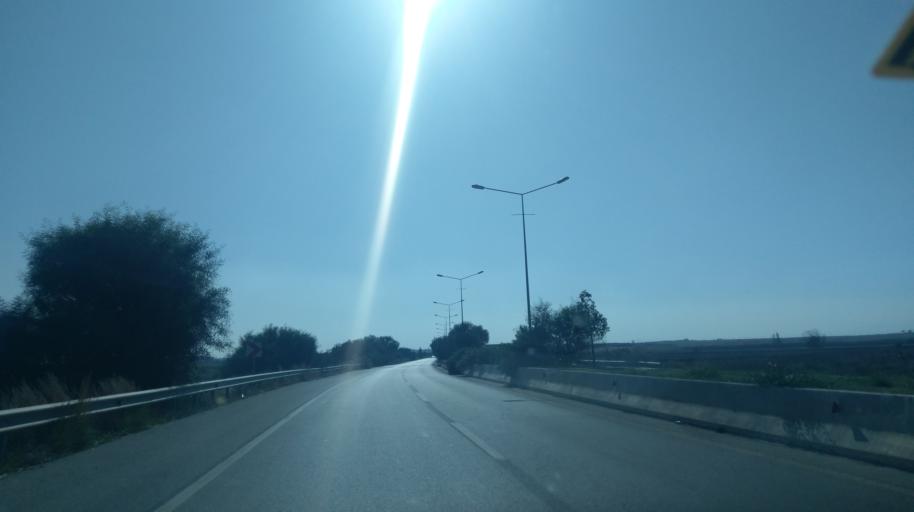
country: CY
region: Lefkosia
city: Geri
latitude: 35.1883
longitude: 33.5031
